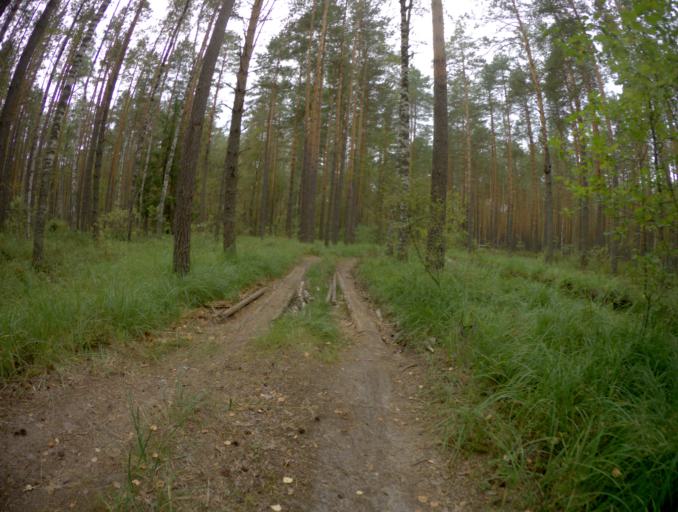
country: RU
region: Vladimir
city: Ivanishchi
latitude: 55.8408
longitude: 40.3283
